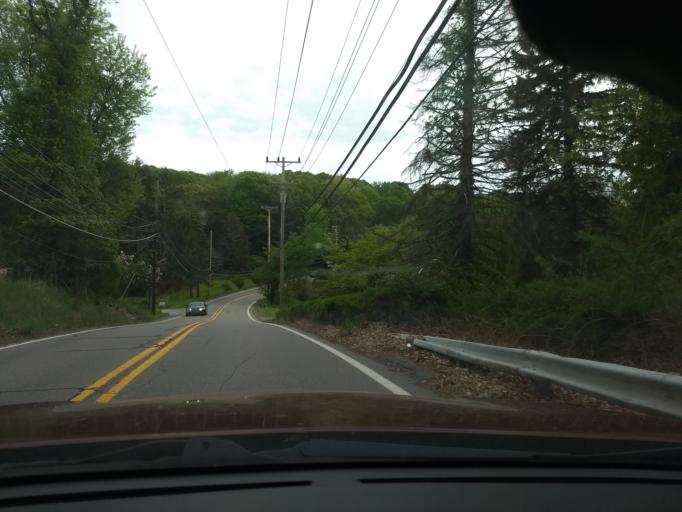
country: US
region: Pennsylvania
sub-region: Allegheny County
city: Coraopolis
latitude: 40.4968
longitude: -80.1329
